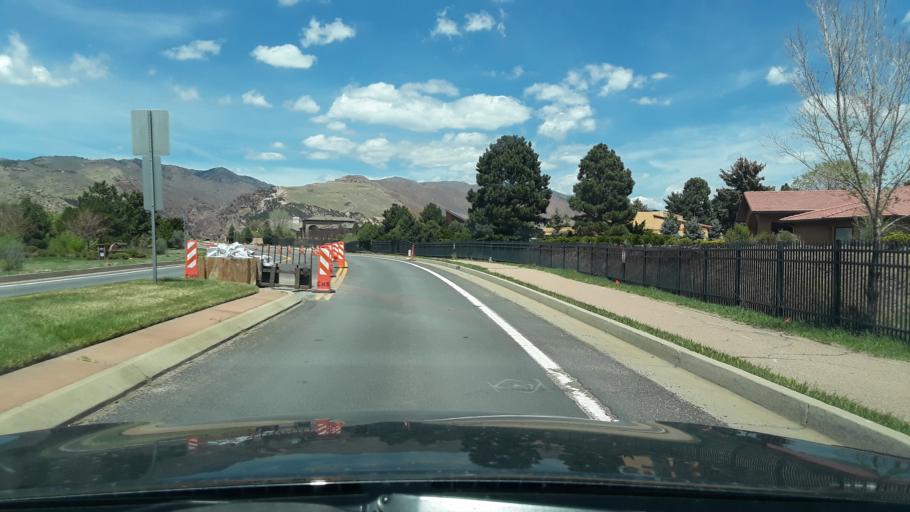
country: US
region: Colorado
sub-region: El Paso County
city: Manitou Springs
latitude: 38.8815
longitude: -104.8689
